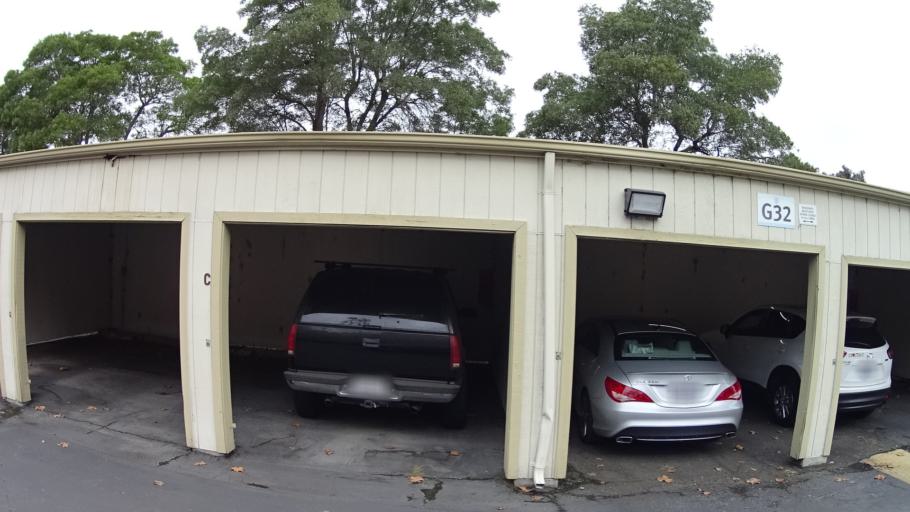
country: US
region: California
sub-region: San Mateo County
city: Belmont
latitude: 37.5336
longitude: -122.2826
